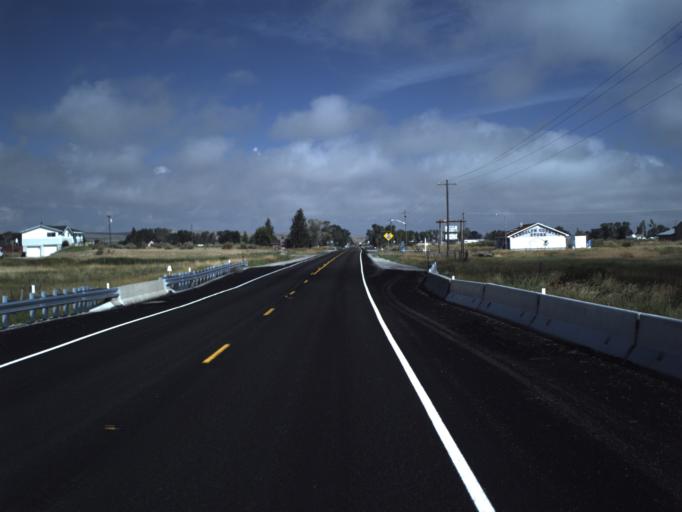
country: US
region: Utah
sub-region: Rich County
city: Randolph
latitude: 41.6542
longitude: -111.1848
